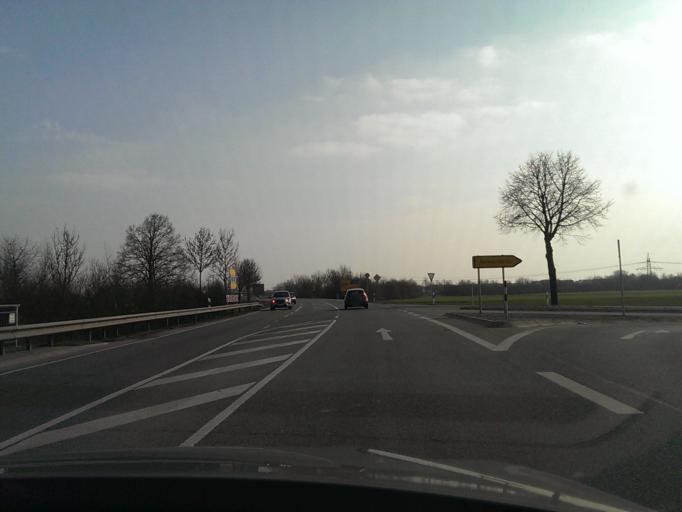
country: DE
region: Bavaria
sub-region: Upper Palatinate
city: Barbing
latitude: 49.0026
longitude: 12.2096
